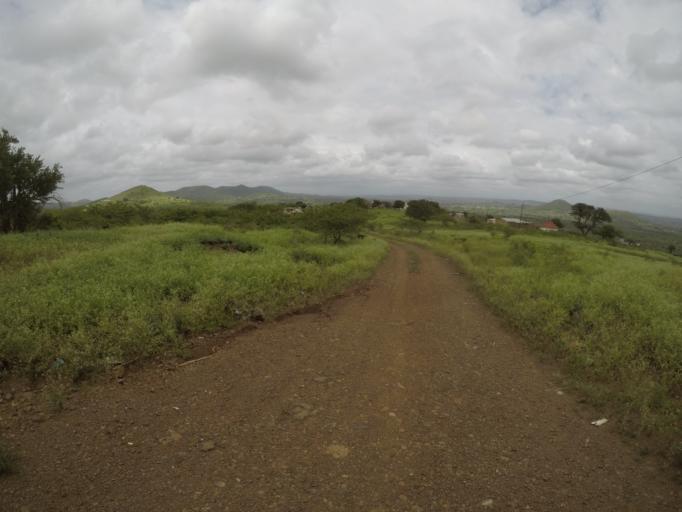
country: ZA
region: KwaZulu-Natal
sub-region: uThungulu District Municipality
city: Empangeni
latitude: -28.6074
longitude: 31.8944
